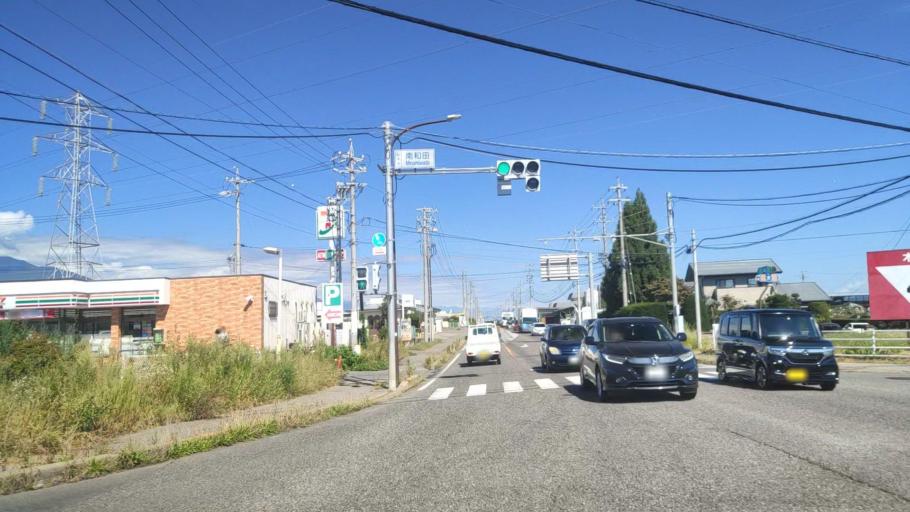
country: JP
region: Nagano
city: Matsumoto
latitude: 36.1960
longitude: 137.9035
